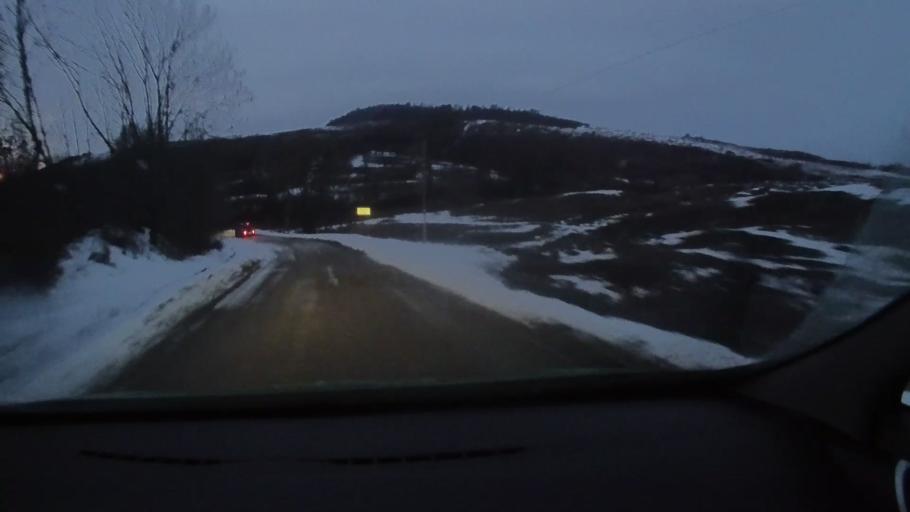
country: RO
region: Harghita
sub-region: Comuna Darjiu
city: Darjiu
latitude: 46.1764
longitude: 25.2423
